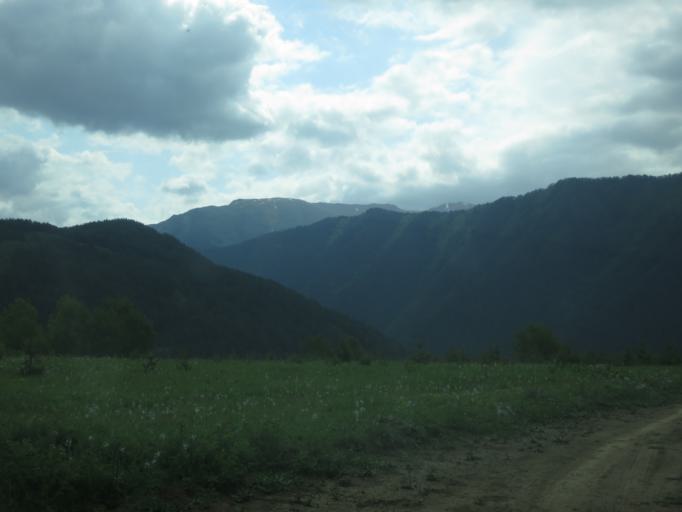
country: RU
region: Chechnya
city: Itum-Kali
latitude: 42.3661
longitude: 45.6409
